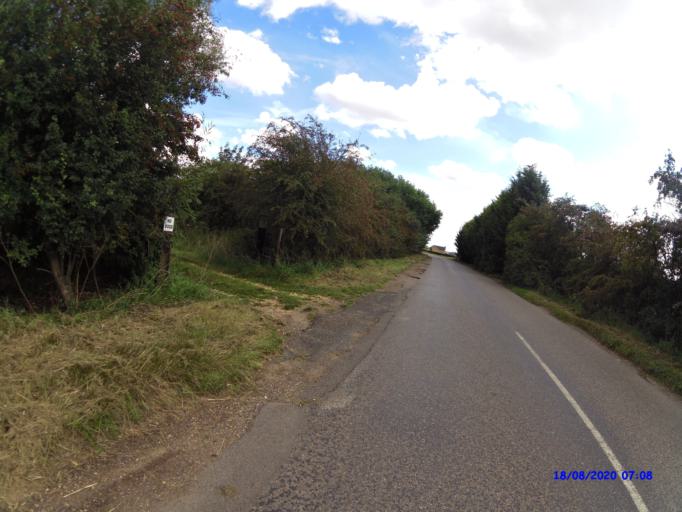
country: GB
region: England
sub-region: Cambridgeshire
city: Whittlesey
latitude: 52.5450
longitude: -0.1131
